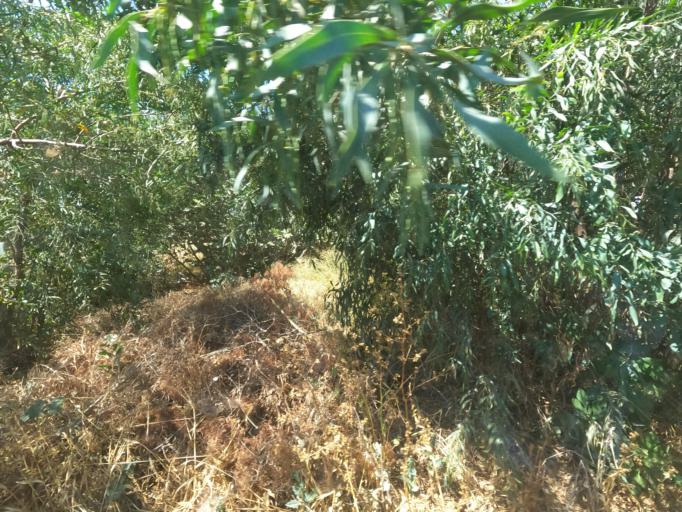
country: CY
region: Ammochostos
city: Liopetri
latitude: 35.0175
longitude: 33.8879
